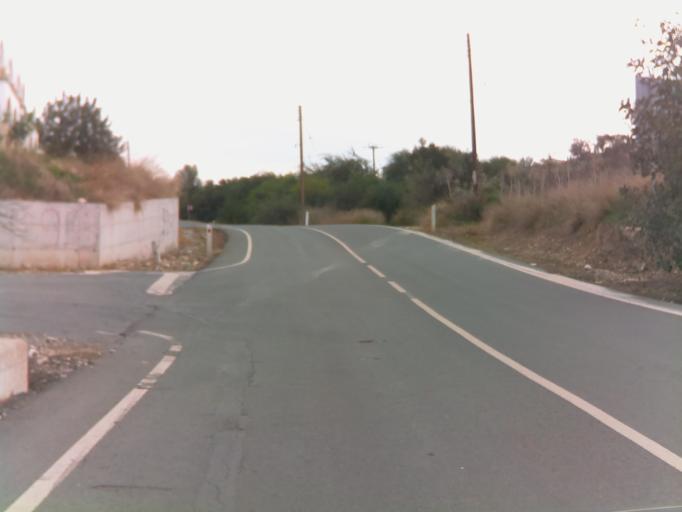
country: CY
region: Pafos
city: Polis
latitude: 35.0386
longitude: 32.3739
